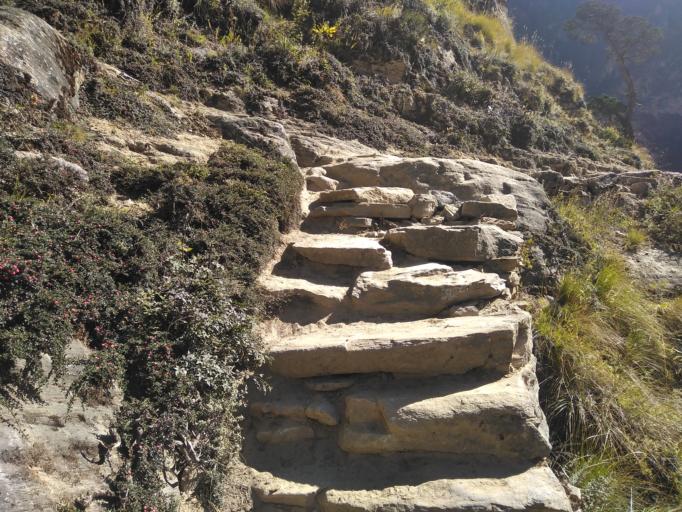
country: NP
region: Western Region
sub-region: Dhawalagiri Zone
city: Jomsom
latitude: 28.9355
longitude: 83.0492
